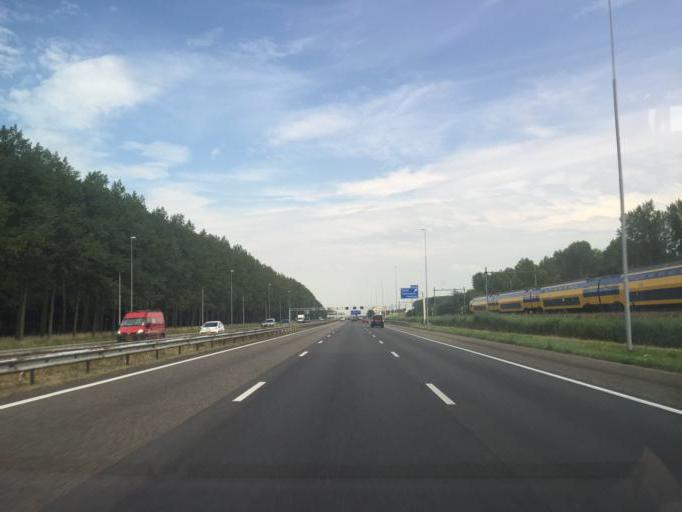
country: NL
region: South Holland
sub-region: Gemeente Pijnacker-Nootdorp
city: Pijnacker
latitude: 52.0506
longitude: 4.4398
